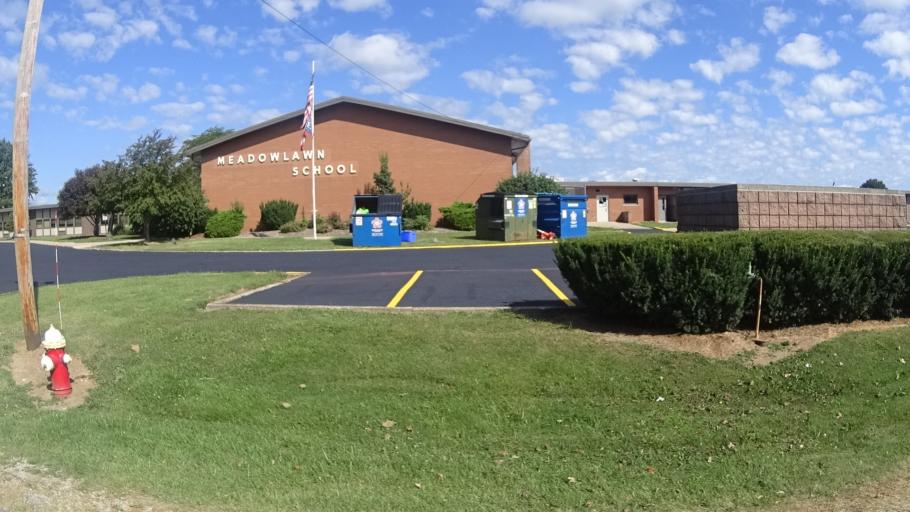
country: US
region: Ohio
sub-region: Erie County
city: Sandusky
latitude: 41.4254
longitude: -82.6706
